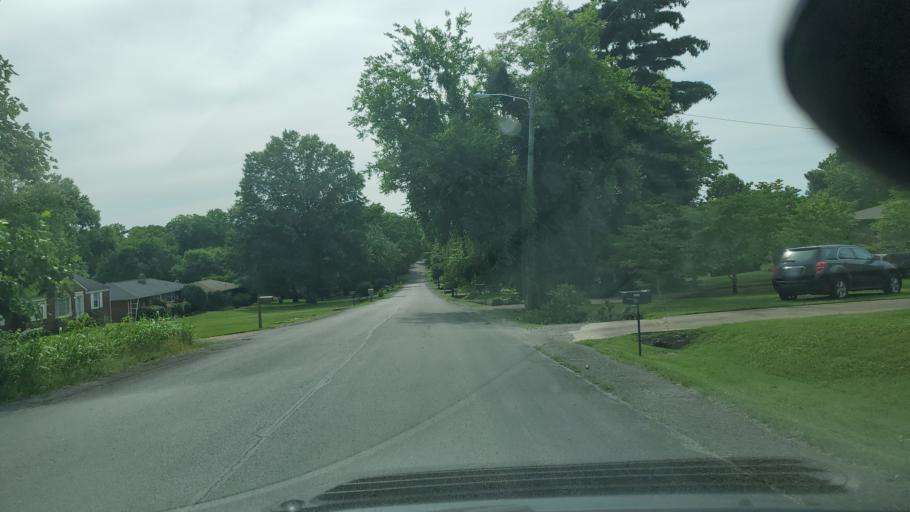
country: US
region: Tennessee
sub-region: Davidson County
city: Lakewood
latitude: 36.1995
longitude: -86.6785
